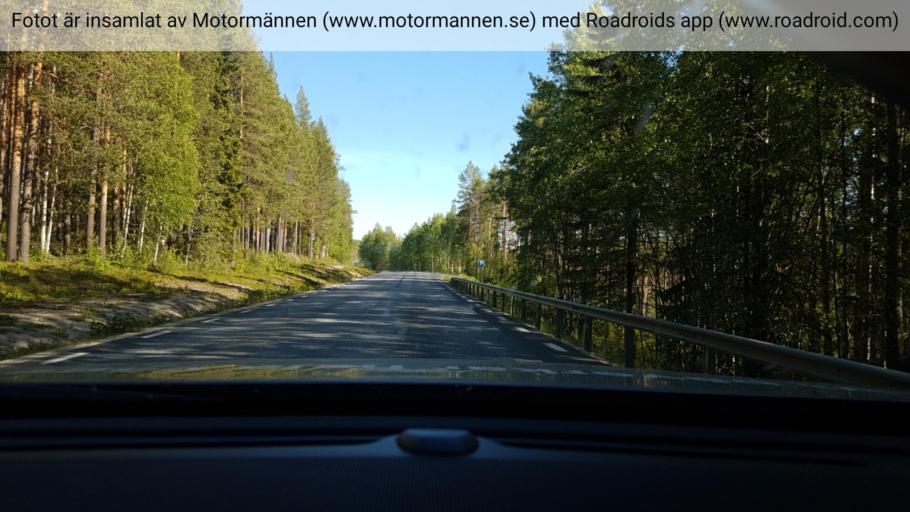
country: SE
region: Vaesterbotten
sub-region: Lycksele Kommun
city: Lycksele
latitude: 64.4192
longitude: 19.0050
